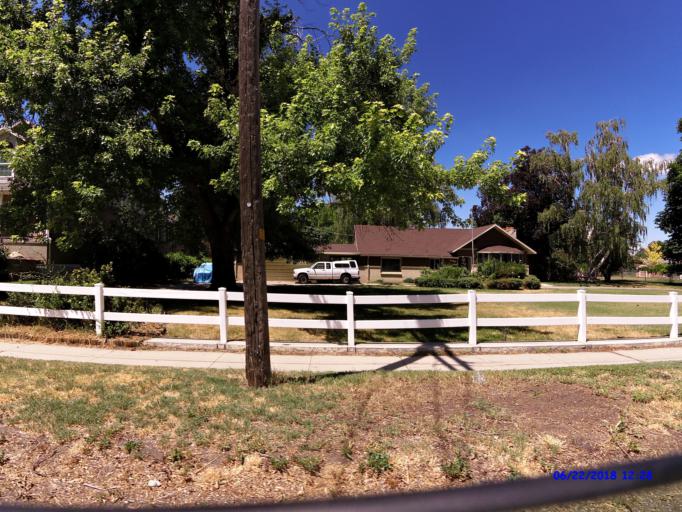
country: US
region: Utah
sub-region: Weber County
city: Ogden
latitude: 41.2411
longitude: -111.9607
